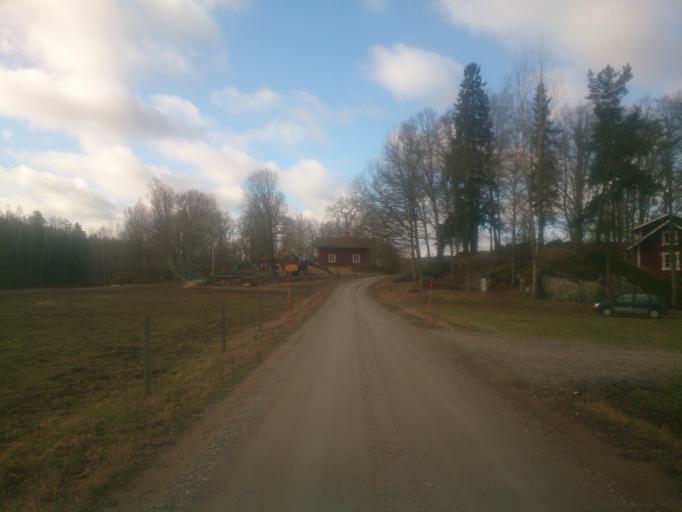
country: SE
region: OEstergoetland
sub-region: Atvidabergs Kommun
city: Atvidaberg
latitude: 58.1938
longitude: 16.1527
